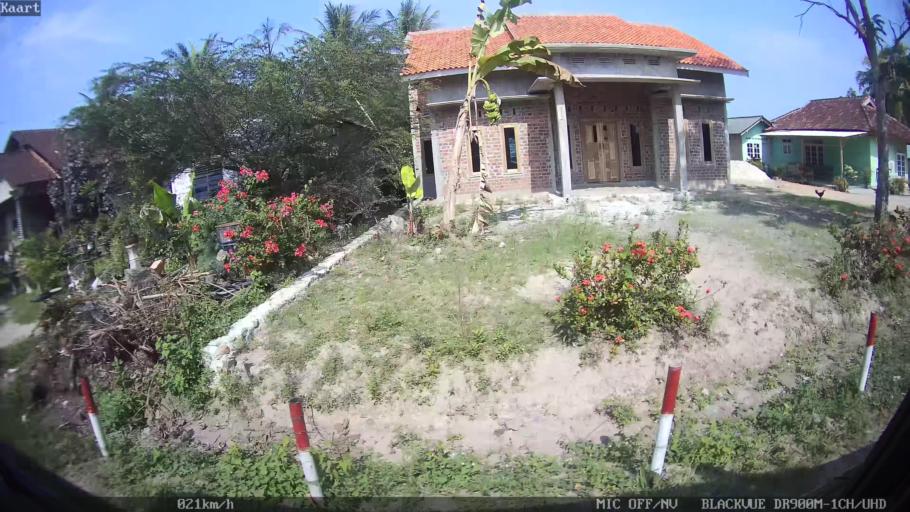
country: ID
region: Lampung
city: Natar
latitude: -5.2610
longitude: 105.2127
